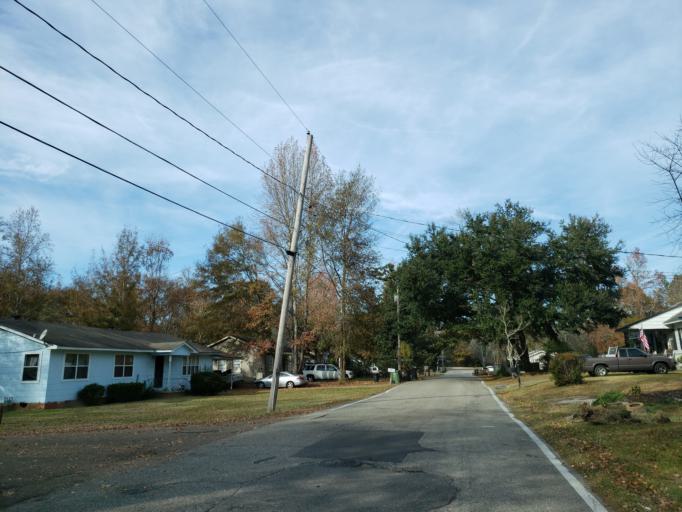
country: US
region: Mississippi
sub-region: Forrest County
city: Hattiesburg
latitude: 31.3342
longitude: -89.3136
